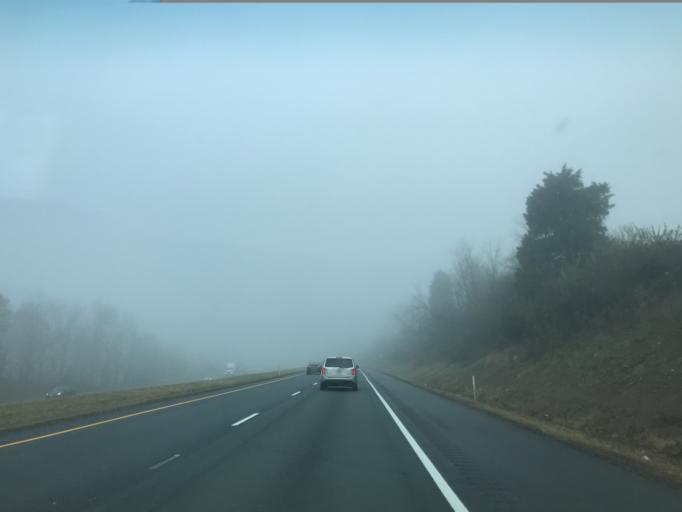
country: US
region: Maryland
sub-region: Washington County
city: Hancock
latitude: 39.6820
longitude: -78.0963
